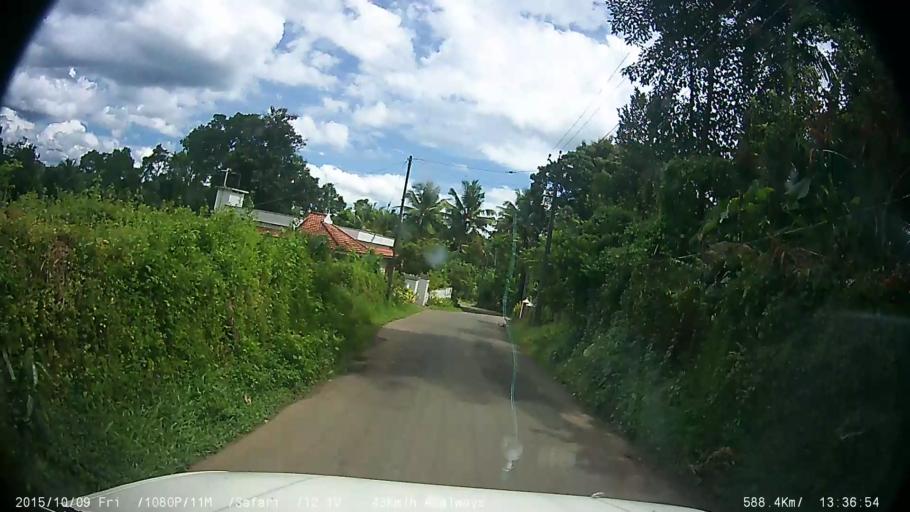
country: IN
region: Kerala
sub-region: Ernakulam
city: Piravam
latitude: 9.8962
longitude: 76.5625
